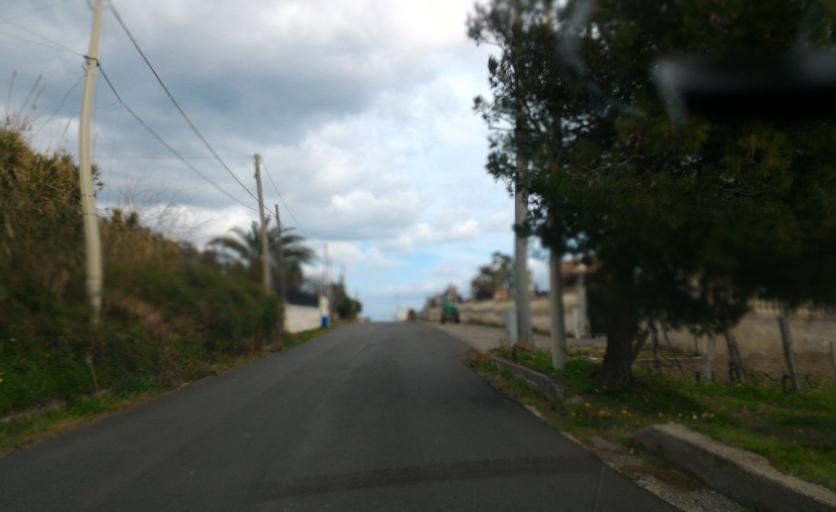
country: IT
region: Calabria
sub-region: Provincia di Crotone
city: Ciro Marina
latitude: 39.3926
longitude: 17.1245
